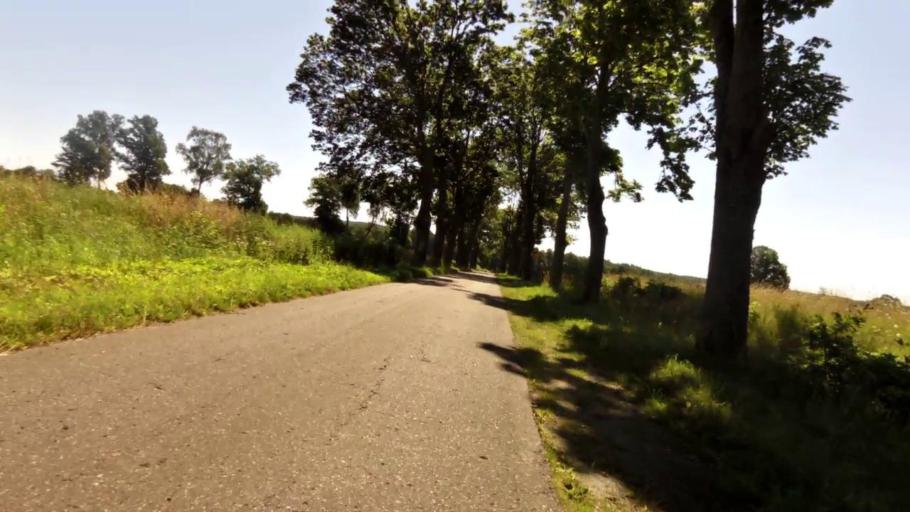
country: PL
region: West Pomeranian Voivodeship
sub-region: Powiat bialogardzki
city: Bialogard
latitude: 53.9379
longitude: 15.9866
